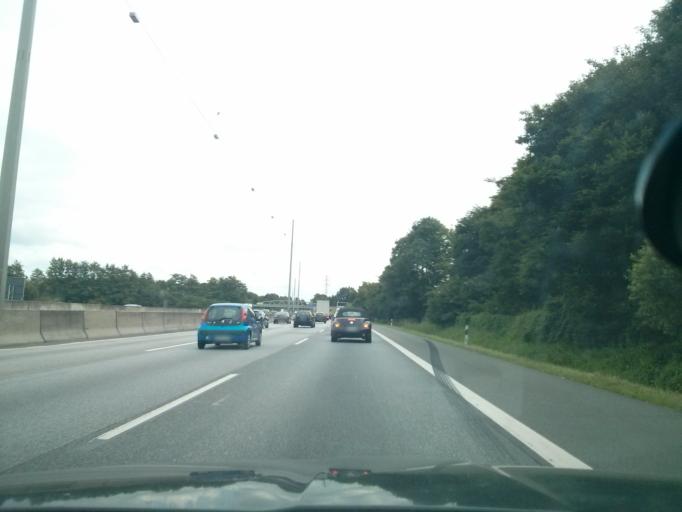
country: DE
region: Hamburg
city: Eidelstedt
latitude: 53.6077
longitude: 9.9182
